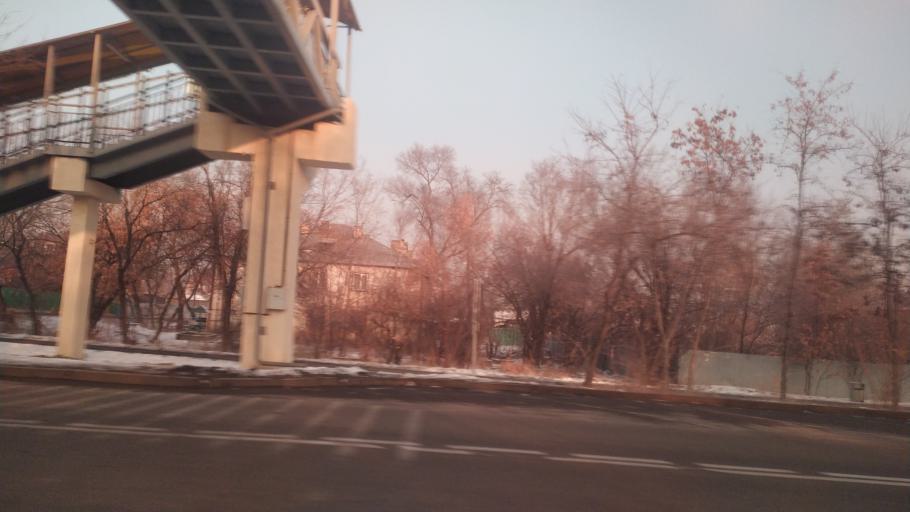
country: KZ
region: Almaty Qalasy
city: Almaty
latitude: 43.2624
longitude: 76.8956
